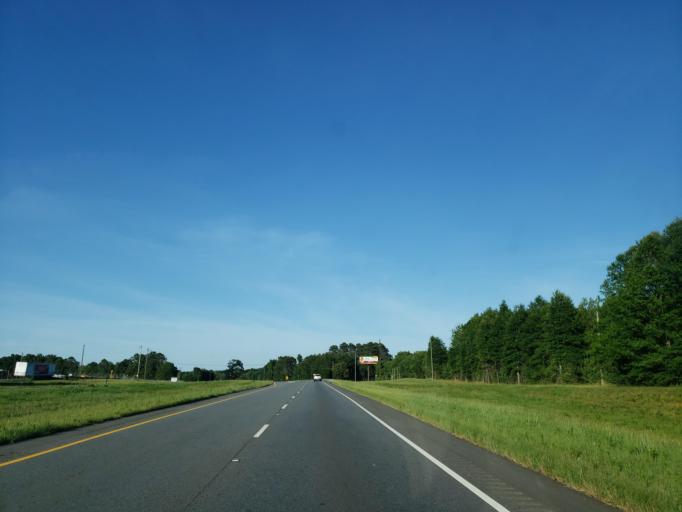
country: US
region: Georgia
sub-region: Floyd County
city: Shannon
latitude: 34.3567
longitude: -85.0618
